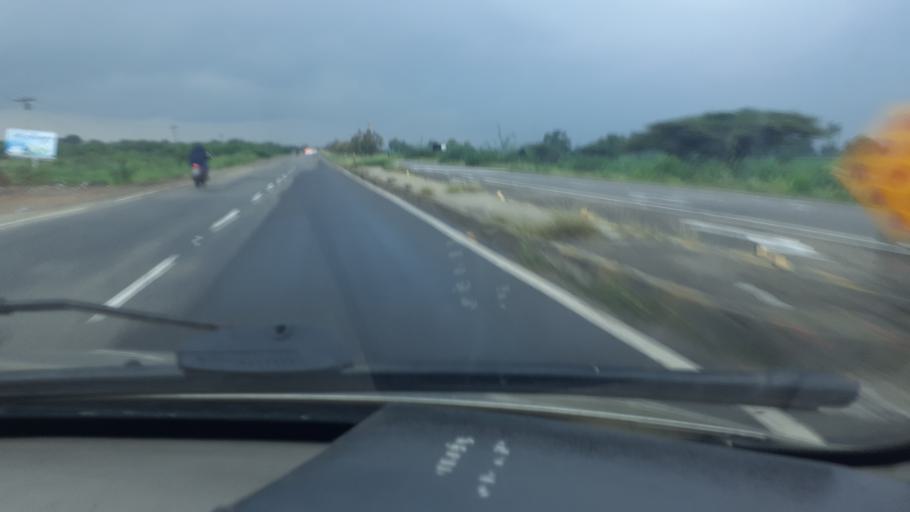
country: IN
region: Tamil Nadu
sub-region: Thoothukkudi
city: Kovilpatti
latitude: 9.1286
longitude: 77.8241
